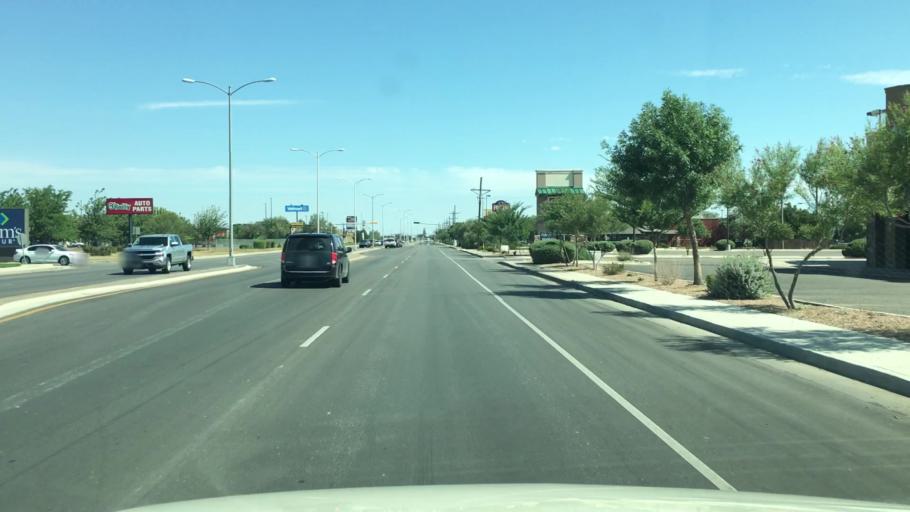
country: US
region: New Mexico
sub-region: Chaves County
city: Roswell
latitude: 33.4466
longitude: -104.5232
